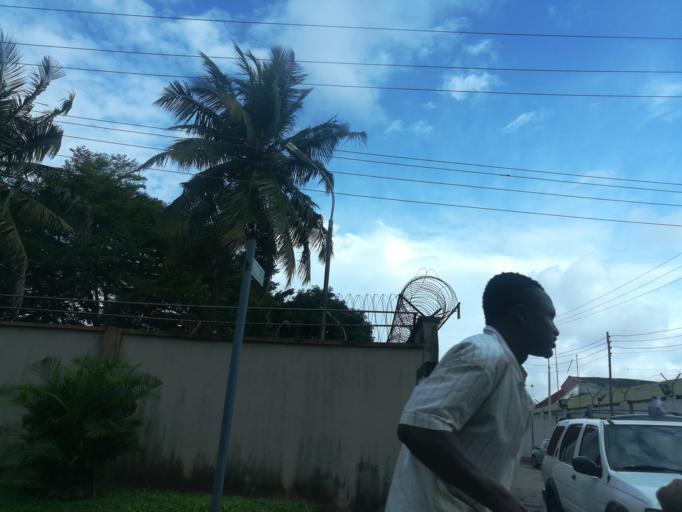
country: NG
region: Lagos
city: Agege
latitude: 6.6202
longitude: 3.3393
